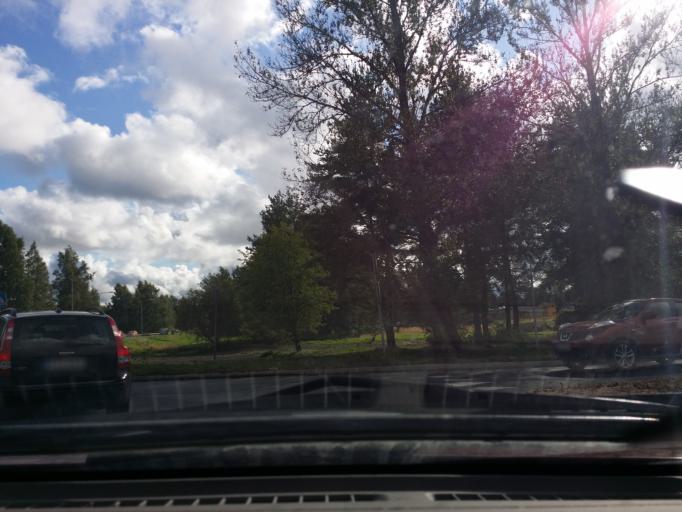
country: FI
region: Satakunta
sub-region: Pori
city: Pori
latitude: 61.4800
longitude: 21.8160
